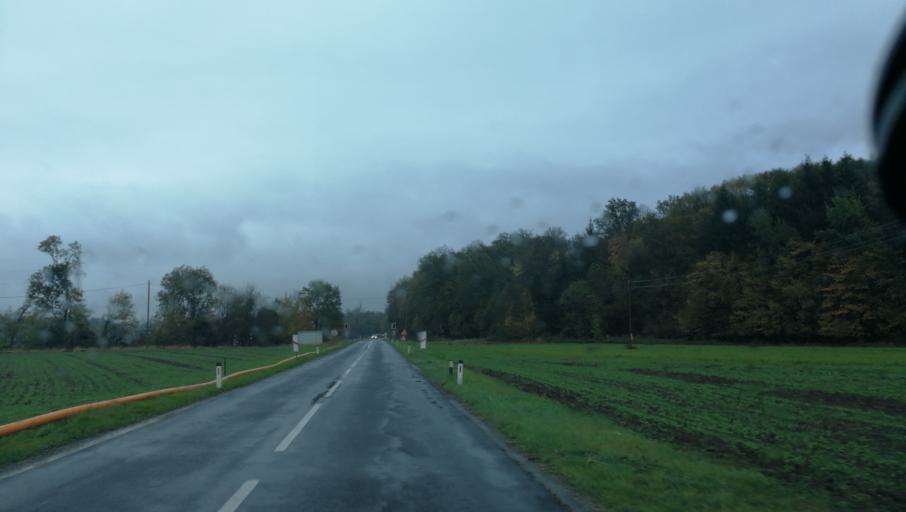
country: AT
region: Styria
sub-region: Politischer Bezirk Leibnitz
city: Spielfeld
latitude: 46.7181
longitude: 15.6436
